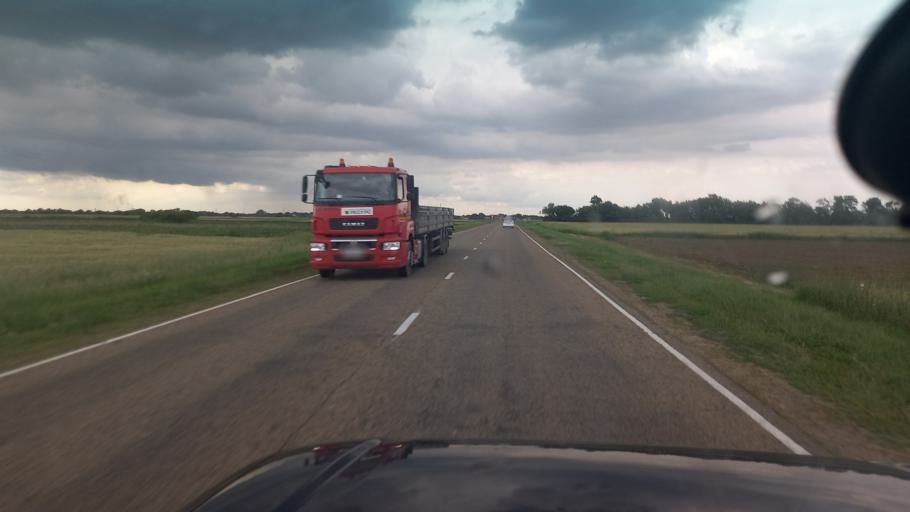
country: RU
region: Adygeya
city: Shovgenovskiy
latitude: 45.0057
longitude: 40.2680
